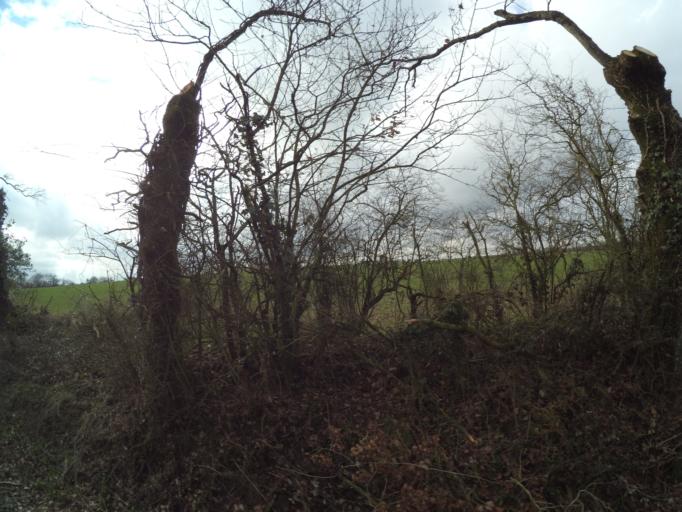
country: FR
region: Pays de la Loire
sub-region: Departement de la Vendee
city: La Bernardiere
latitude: 47.0232
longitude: -1.2922
